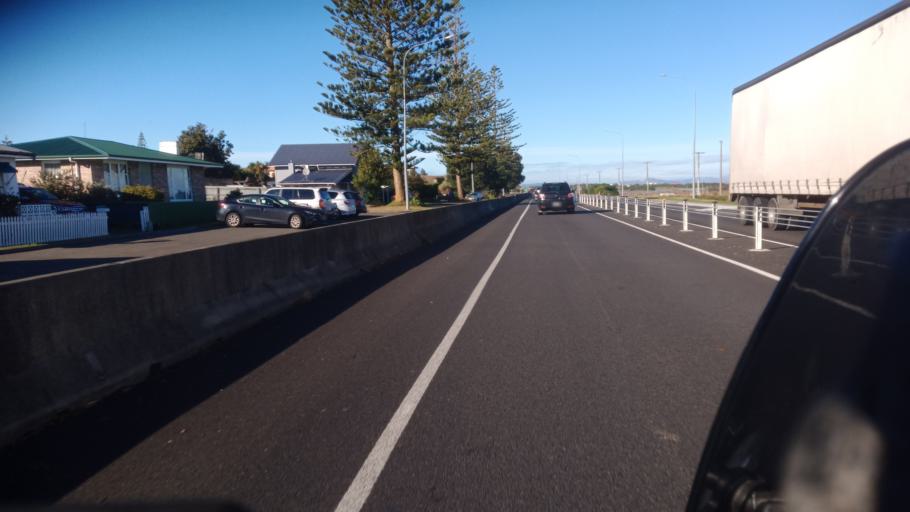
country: NZ
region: Hawke's Bay
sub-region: Napier City
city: Napier
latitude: -39.4656
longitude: 176.8747
